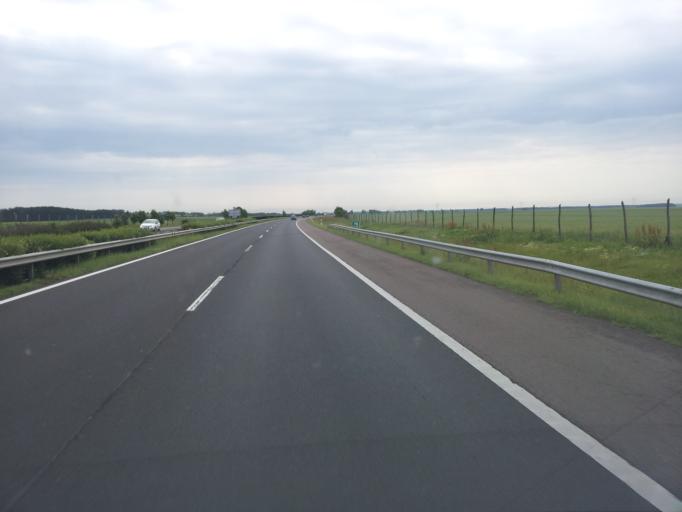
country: HU
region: Heves
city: Adacs
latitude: 47.7297
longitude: 19.9721
